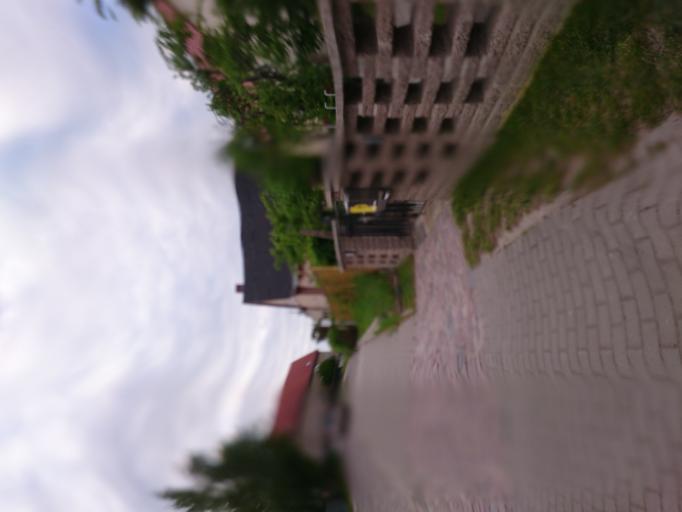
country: DE
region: Berlin
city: Blankenfelde
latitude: 52.6167
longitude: 13.3855
